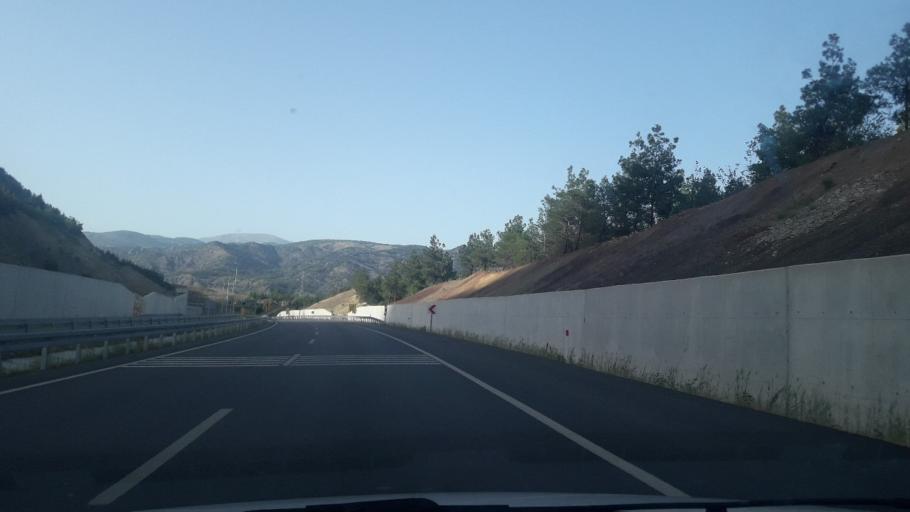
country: TR
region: Amasya
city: Amasya
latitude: 40.6817
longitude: 35.8118
